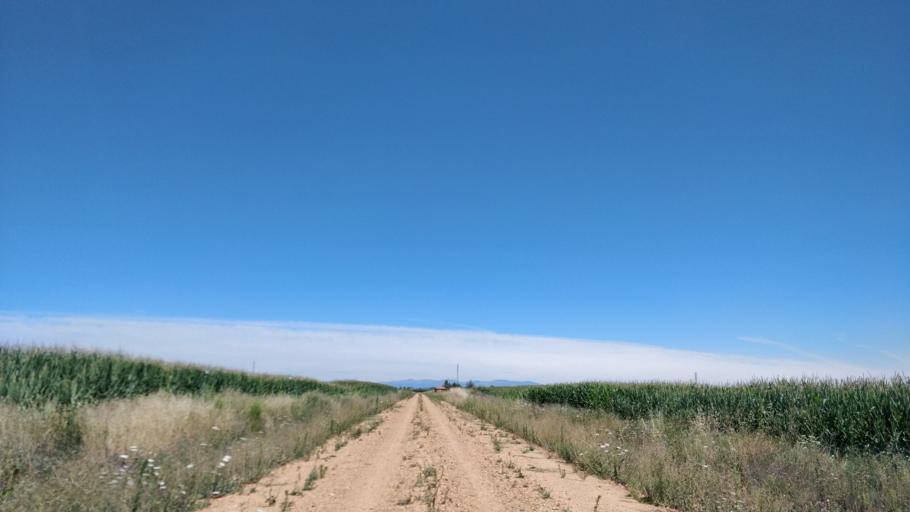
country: ES
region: Castille and Leon
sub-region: Provincia de Leon
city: Bustillo del Paramo
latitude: 42.4551
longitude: -5.8166
